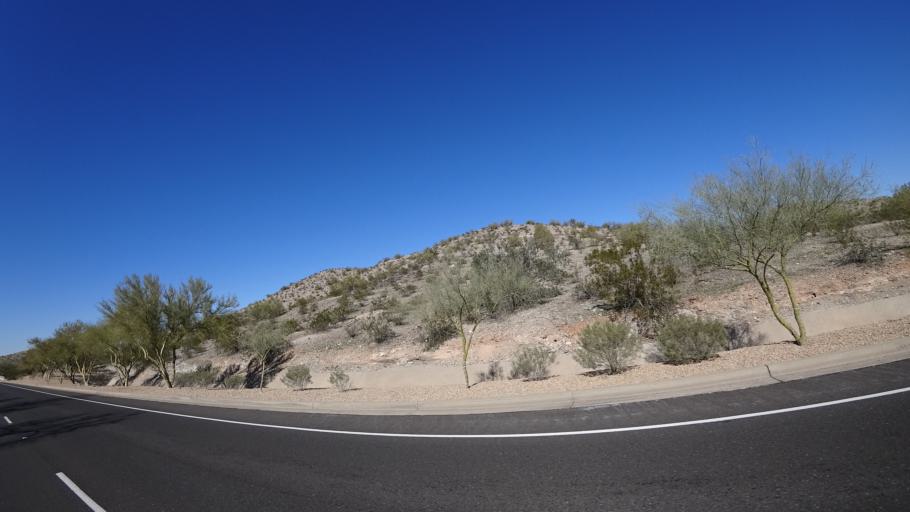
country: US
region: Arizona
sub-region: Maricopa County
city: Goodyear
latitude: 33.3549
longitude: -112.4372
